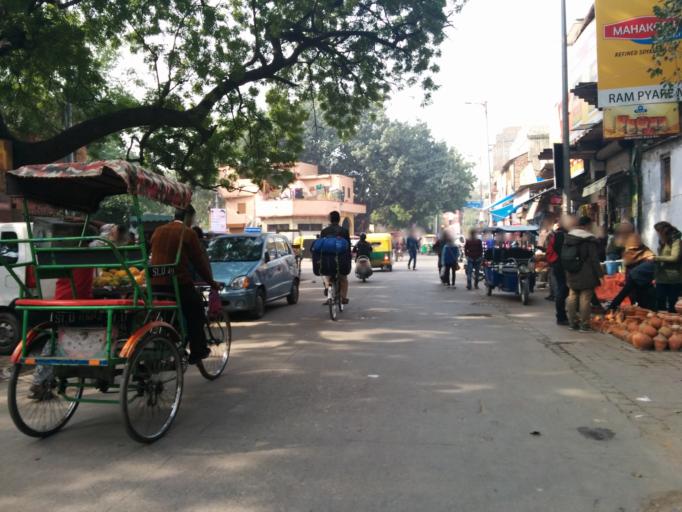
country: IN
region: NCT
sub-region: New Delhi
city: New Delhi
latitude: 28.6404
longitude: 77.2096
